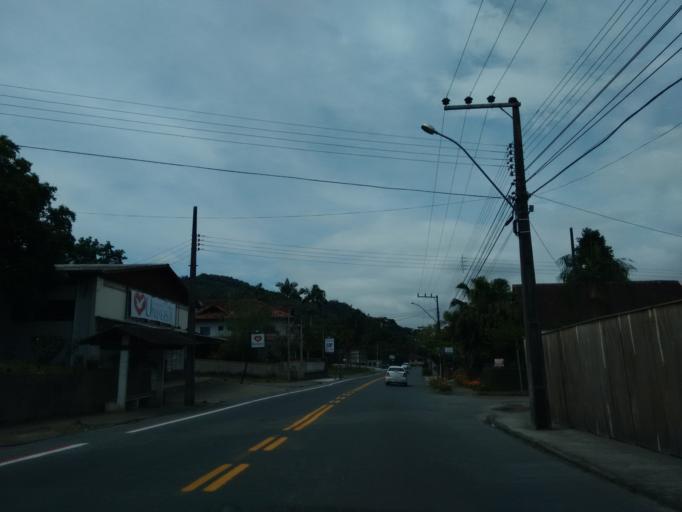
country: BR
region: Santa Catarina
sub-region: Pomerode
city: Pomerode
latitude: -26.7181
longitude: -49.1676
